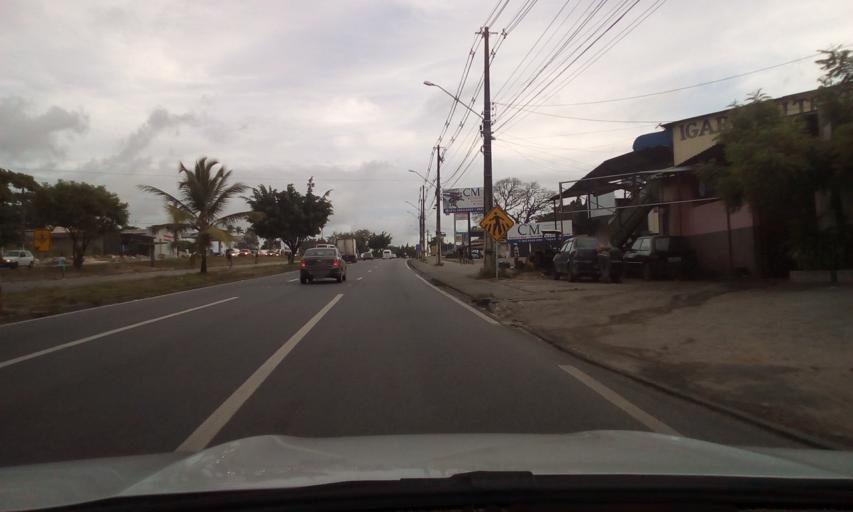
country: BR
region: Pernambuco
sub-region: Igarassu
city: Igarassu
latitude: -7.8468
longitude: -34.9102
